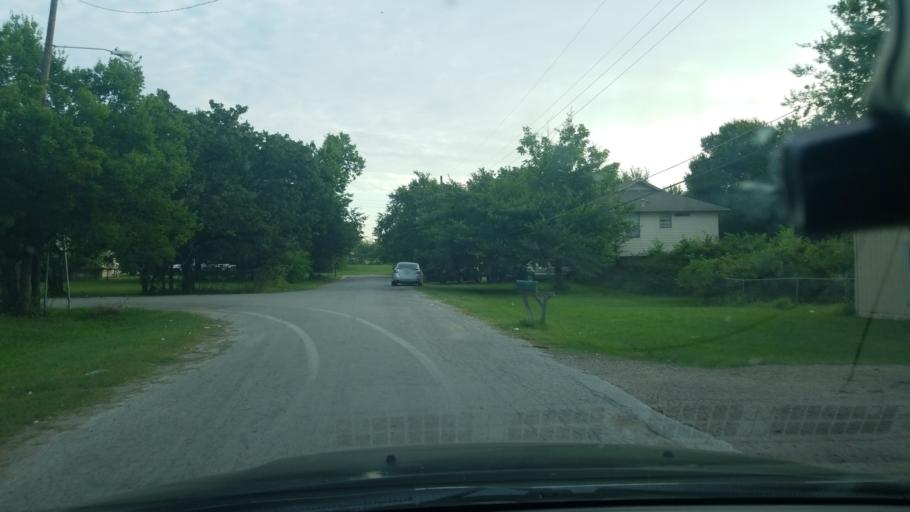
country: US
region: Texas
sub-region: Dallas County
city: Balch Springs
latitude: 32.7359
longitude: -96.6297
